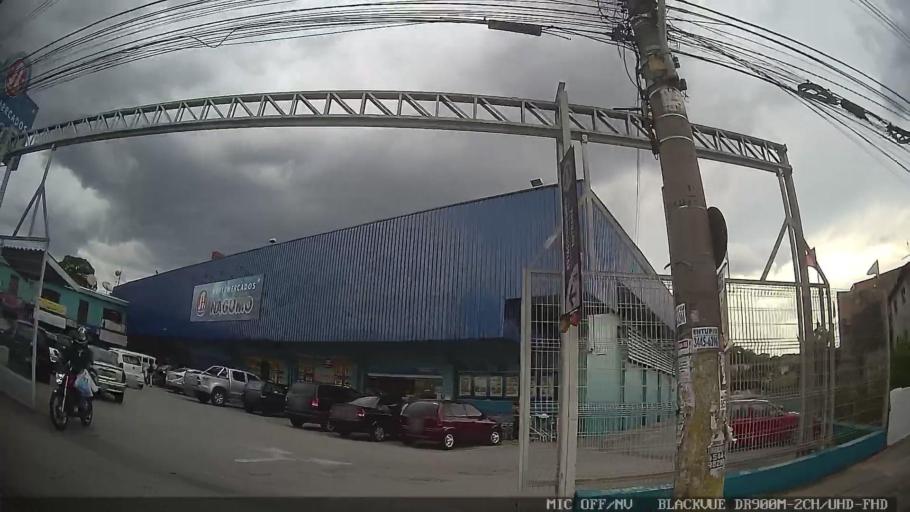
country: BR
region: Sao Paulo
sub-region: Maua
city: Maua
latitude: -23.6650
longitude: -46.4315
